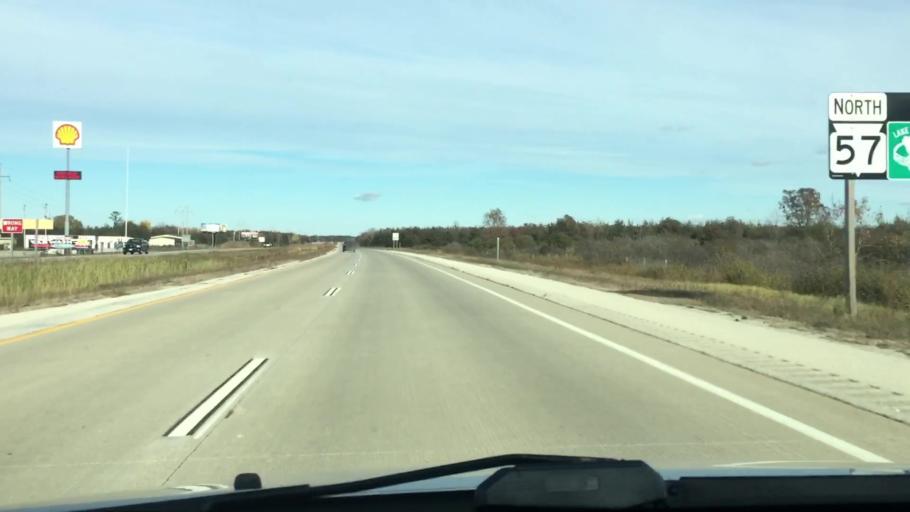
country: US
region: Wisconsin
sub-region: Kewaunee County
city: Luxemburg
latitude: 44.6203
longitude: -87.8241
